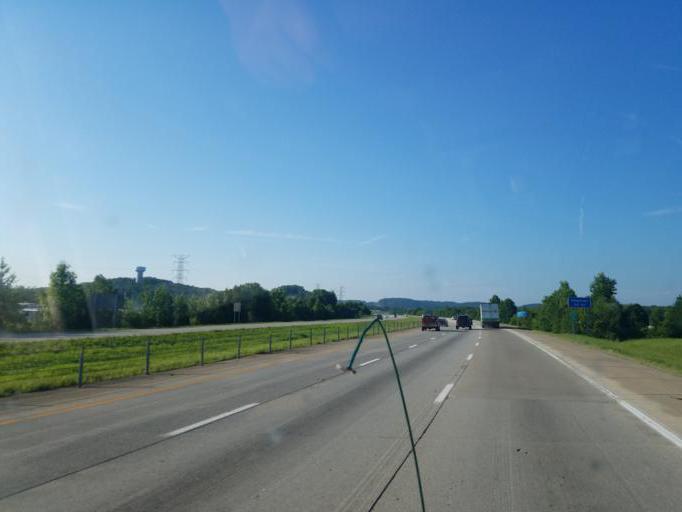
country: US
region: Kentucky
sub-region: Bullitt County
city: Shepherdsville
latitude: 37.9126
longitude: -85.6878
